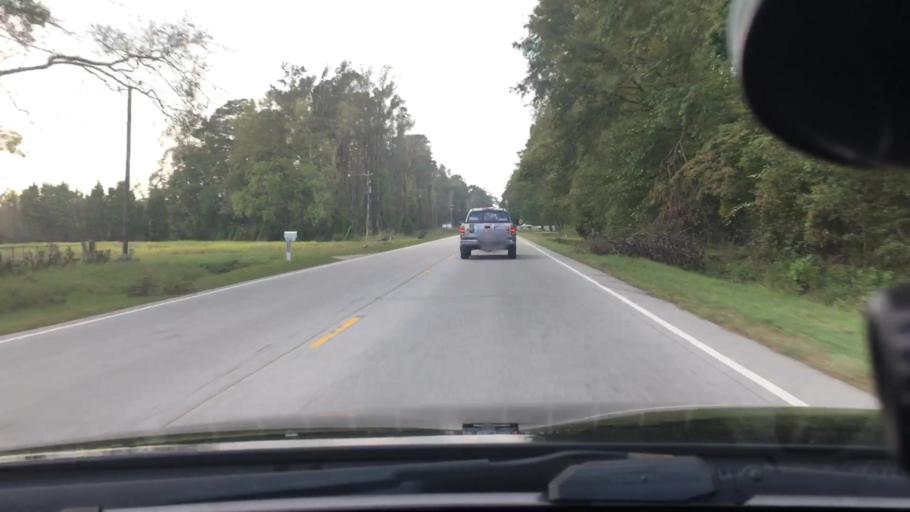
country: US
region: North Carolina
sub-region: Craven County
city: Vanceboro
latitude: 35.2596
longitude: -77.0997
